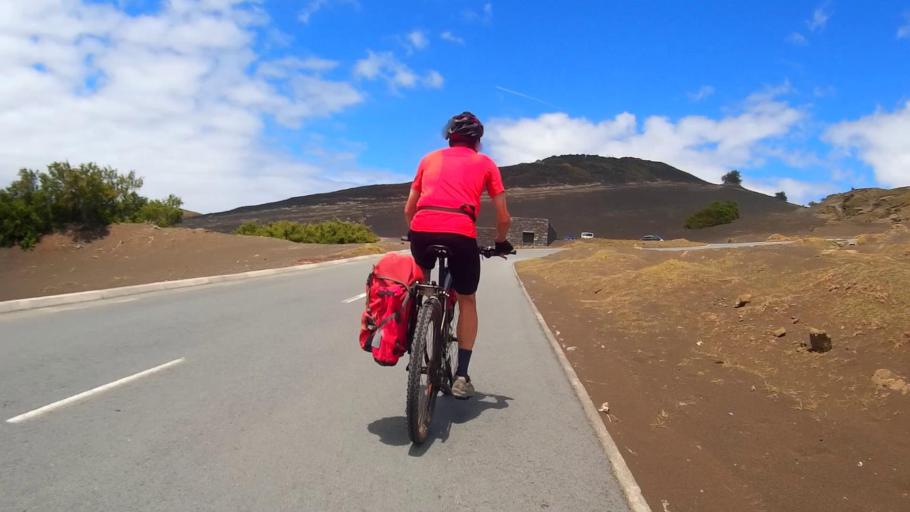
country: PT
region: Azores
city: Ribeira Grande
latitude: 38.5958
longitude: -28.8232
